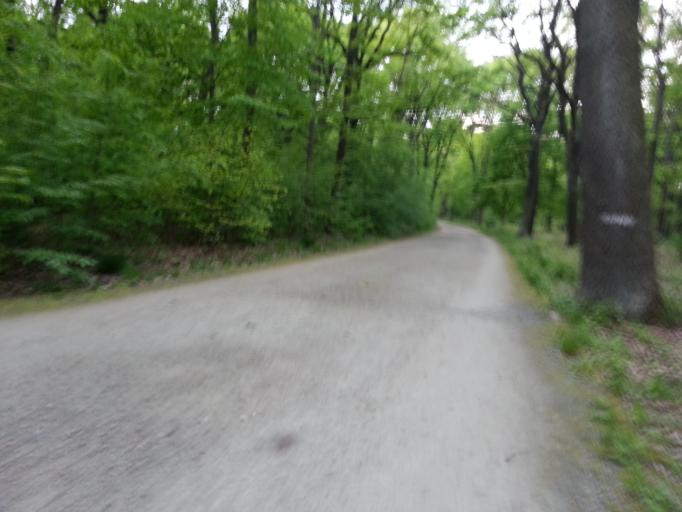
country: DE
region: Berlin
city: Charlottenburg-Nord
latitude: 52.5468
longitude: 13.2938
